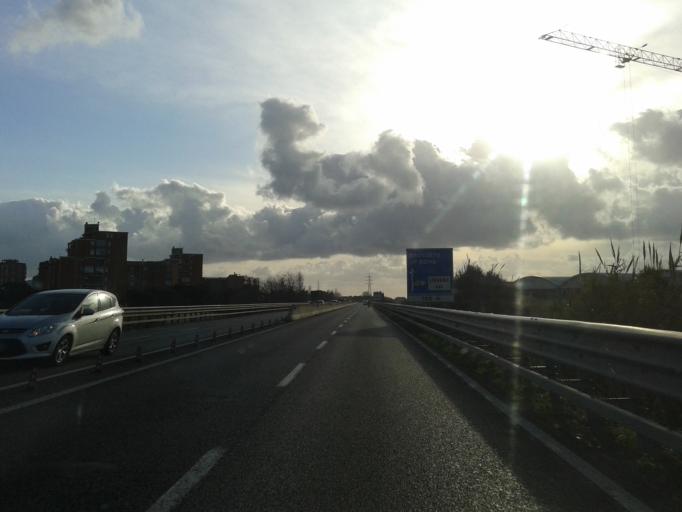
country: IT
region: Tuscany
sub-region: Provincia di Livorno
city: Livorno
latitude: 43.5413
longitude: 10.3380
